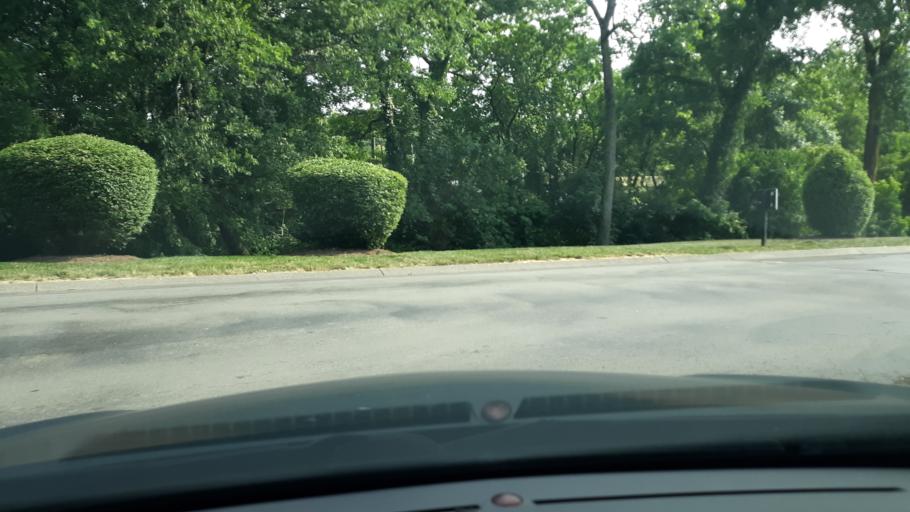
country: US
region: Tennessee
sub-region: Davidson County
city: Lakewood
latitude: 36.1837
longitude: -86.6073
